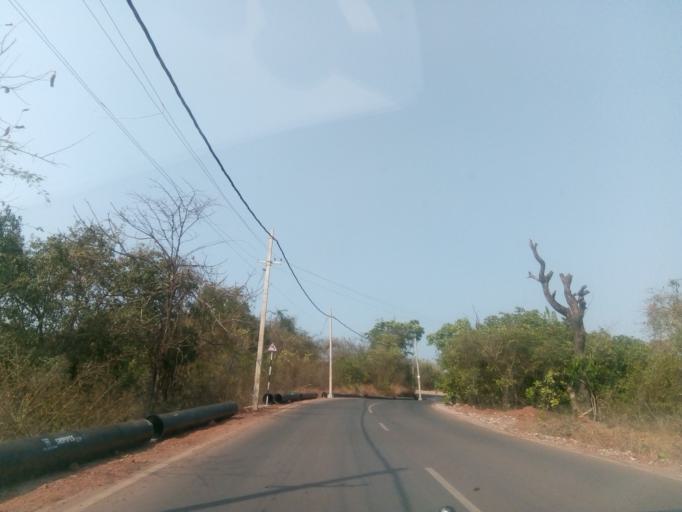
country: IN
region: Goa
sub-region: North Goa
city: Pernem
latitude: 15.7214
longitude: 73.8533
